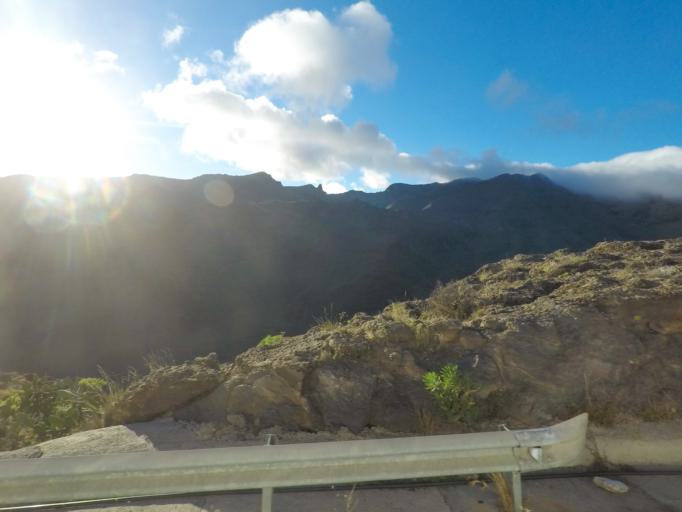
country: ES
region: Canary Islands
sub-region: Provincia de Santa Cruz de Tenerife
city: Alajero
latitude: 28.0770
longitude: -17.2089
